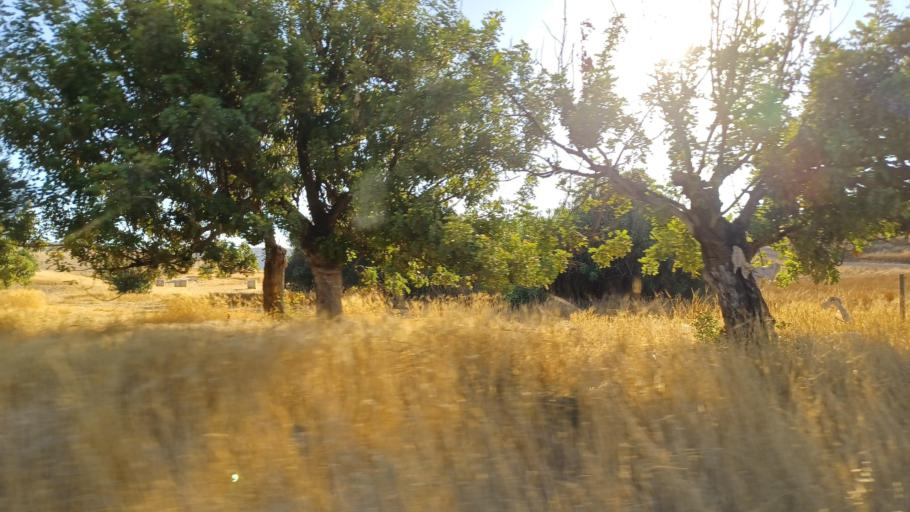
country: CY
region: Larnaka
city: Troulloi
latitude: 35.0298
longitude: 33.6277
